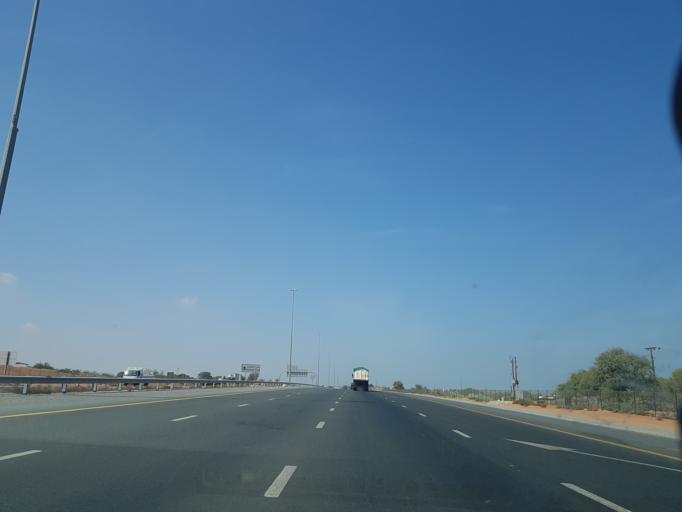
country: AE
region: Ra's al Khaymah
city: Ras al-Khaimah
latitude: 25.7037
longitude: 55.9553
